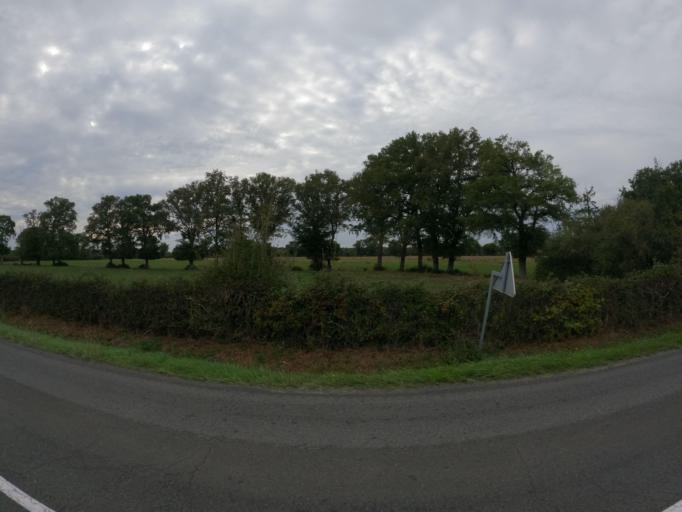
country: FR
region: Poitou-Charentes
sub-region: Departement de la Vienne
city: Saulge
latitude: 46.3547
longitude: 0.8336
